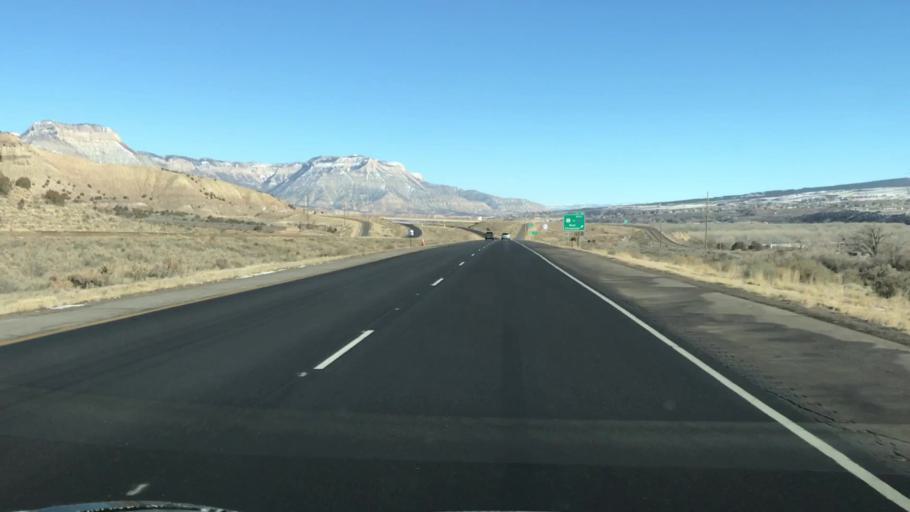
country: US
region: Colorado
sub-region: Garfield County
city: Parachute
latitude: 39.4231
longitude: -108.0851
